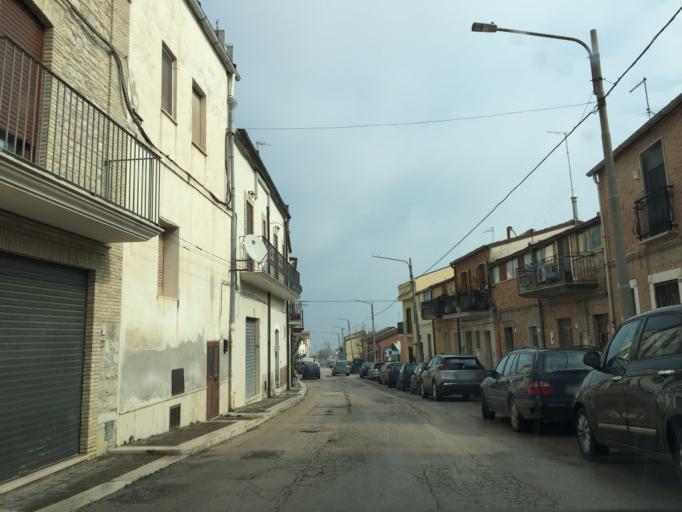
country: IT
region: Apulia
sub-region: Provincia di Foggia
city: Troia
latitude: 41.3600
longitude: 15.3086
